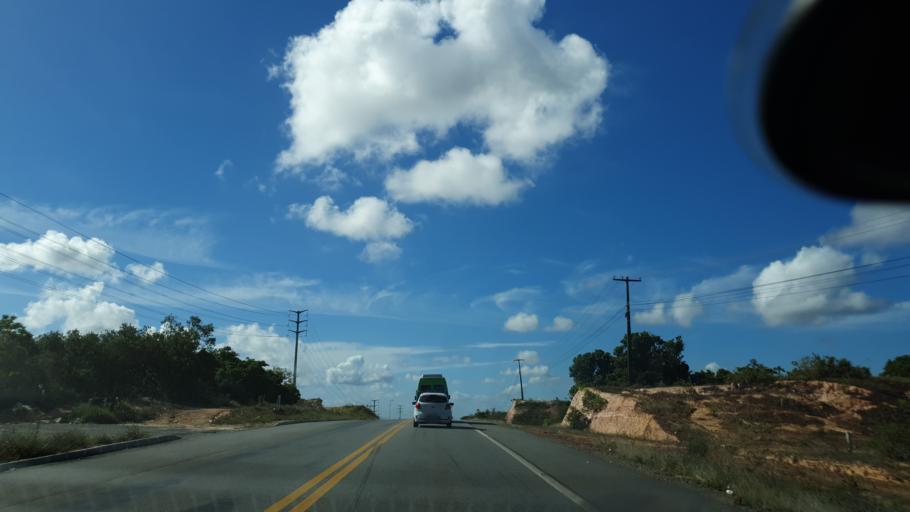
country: BR
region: Bahia
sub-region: Camacari
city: Camacari
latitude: -12.6948
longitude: -38.2223
